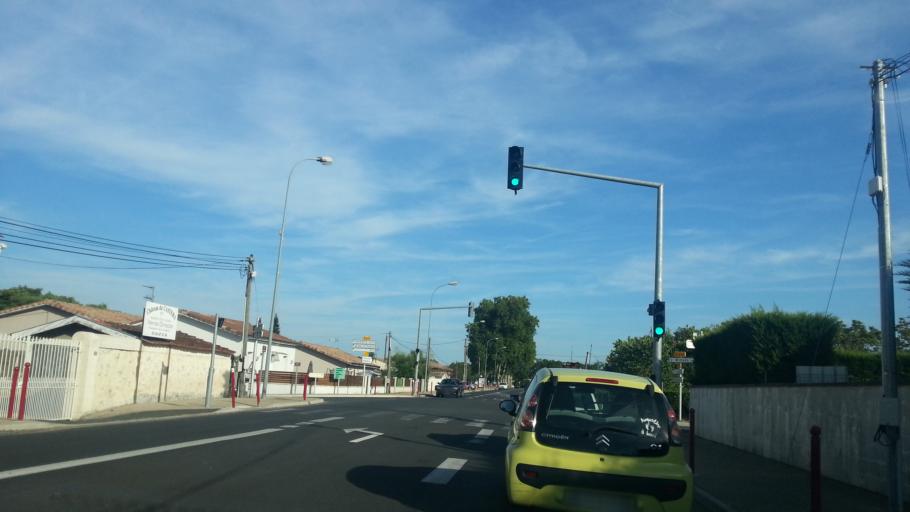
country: FR
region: Aquitaine
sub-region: Departement de la Gironde
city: Paillet
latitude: 44.6741
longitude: -0.3978
